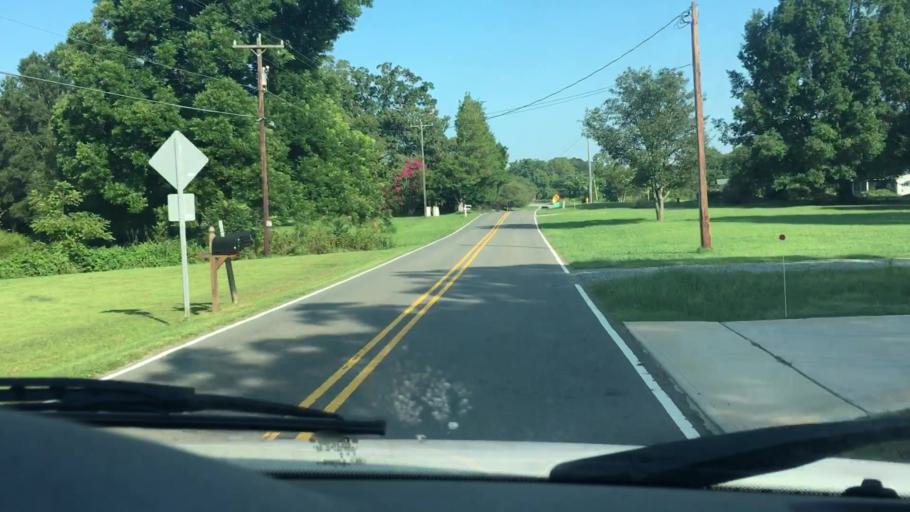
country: US
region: North Carolina
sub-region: Mecklenburg County
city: Huntersville
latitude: 35.4370
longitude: -80.8146
